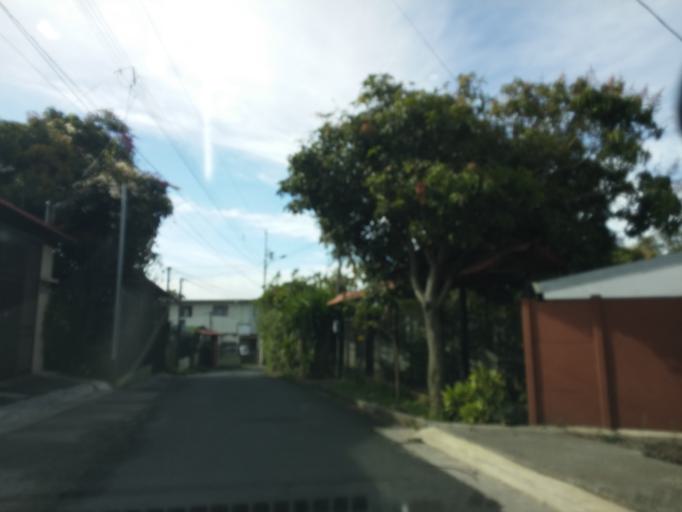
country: CR
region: Heredia
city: San Francisco
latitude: 9.9928
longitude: -84.1366
